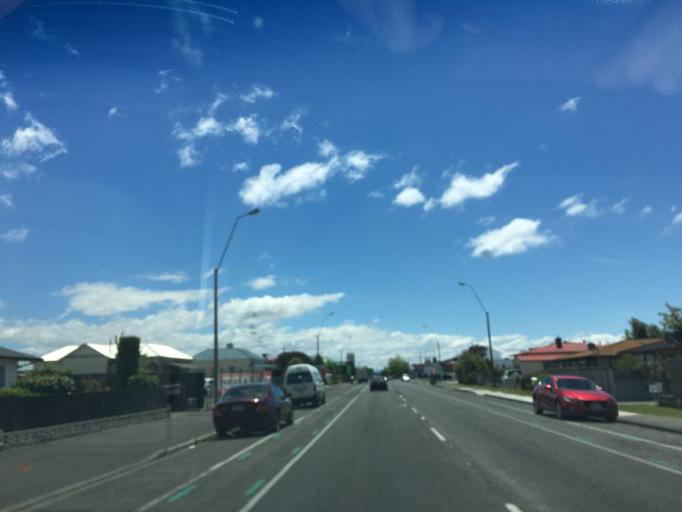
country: NZ
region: Hawke's Bay
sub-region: Hastings District
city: Hastings
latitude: -39.6443
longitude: 176.8512
